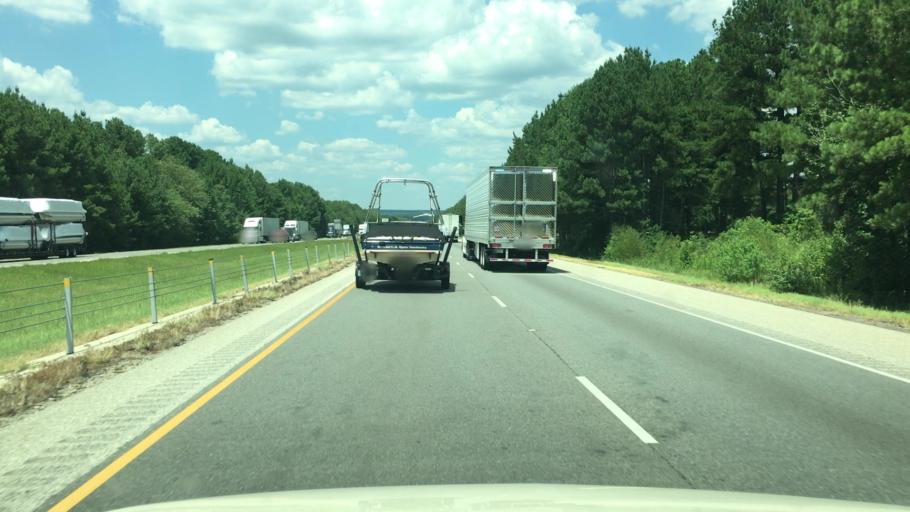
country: US
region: Arkansas
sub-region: Clark County
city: Arkadelphia
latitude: 34.1511
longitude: -93.0784
